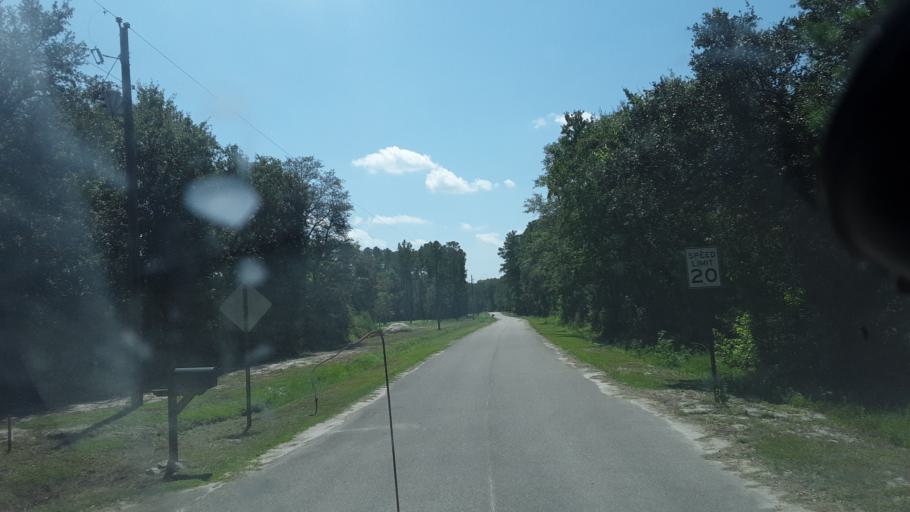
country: US
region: South Carolina
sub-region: Horry County
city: Forestbrook
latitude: 33.8407
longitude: -78.8625
